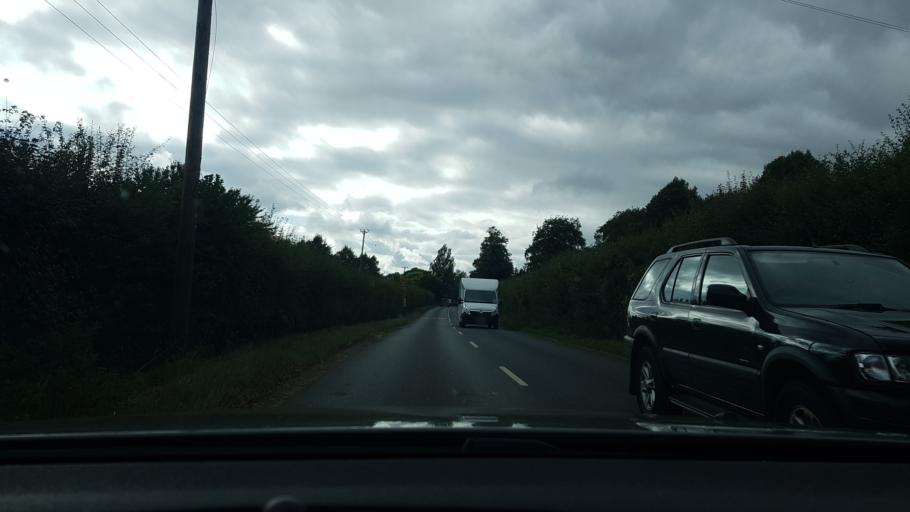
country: GB
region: England
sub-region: West Berkshire
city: Hermitage
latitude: 51.4581
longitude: -1.2998
